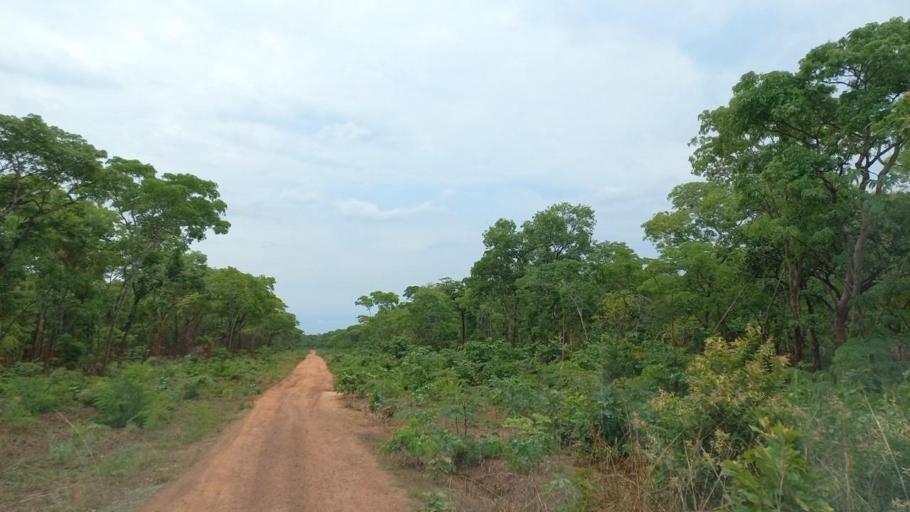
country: ZM
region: North-Western
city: Kalengwa
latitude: -13.6247
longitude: 24.9774
